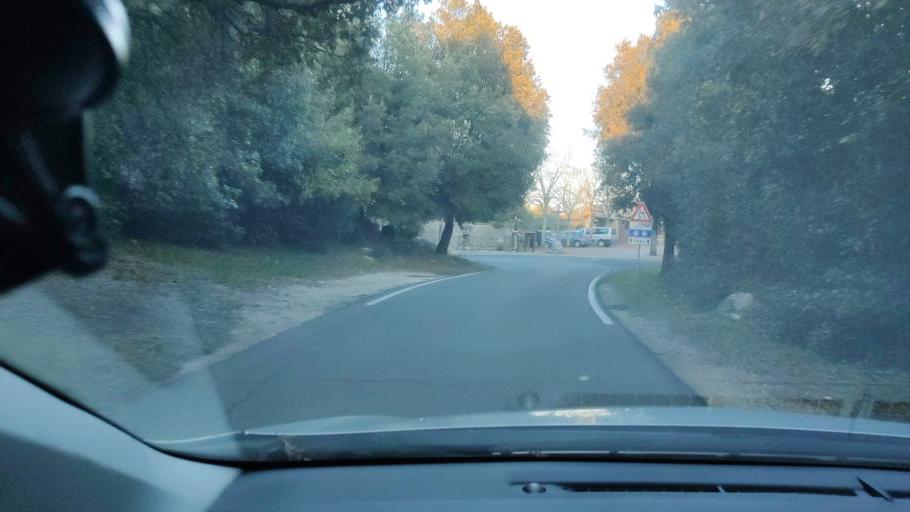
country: IT
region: Umbria
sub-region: Provincia di Terni
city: Amelia
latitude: 42.5835
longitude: 12.4320
